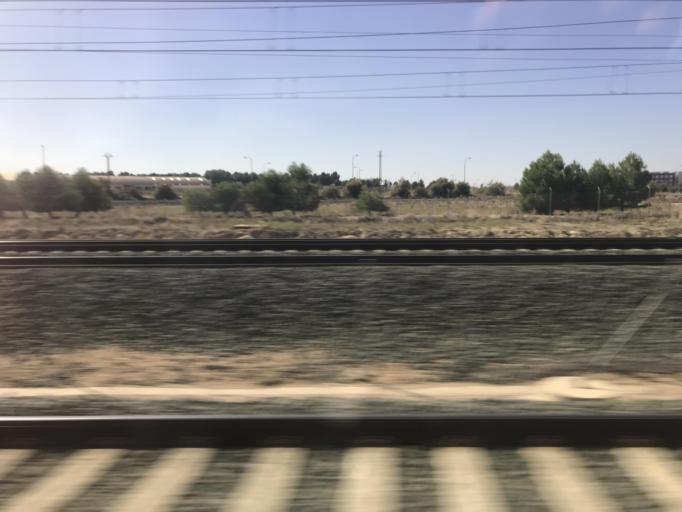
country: ES
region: Castille-La Mancha
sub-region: Provincia de Albacete
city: Albacete
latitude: 39.0151
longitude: -1.8626
